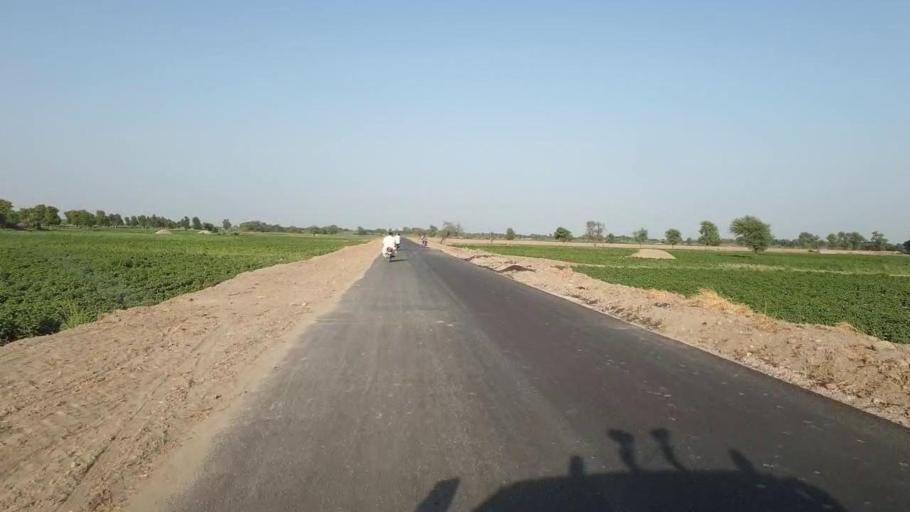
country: PK
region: Sindh
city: Jam Sahib
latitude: 26.3416
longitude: 68.5693
